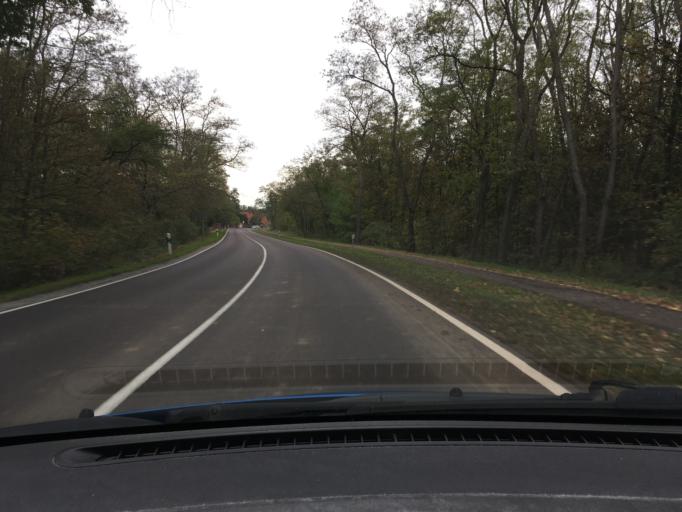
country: DE
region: Saxony-Anhalt
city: Biederitz
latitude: 52.1349
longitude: 11.7511
